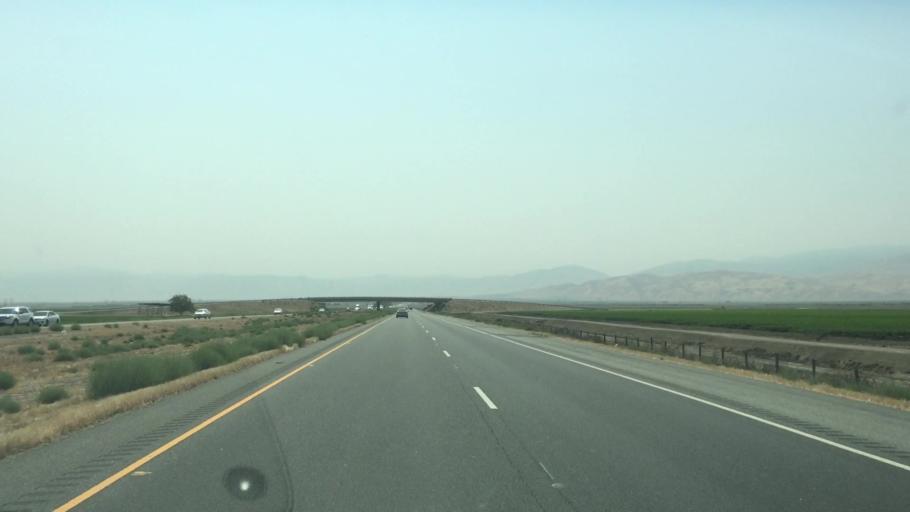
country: US
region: California
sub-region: Kern County
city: Greenfield
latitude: 35.1324
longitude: -119.0787
